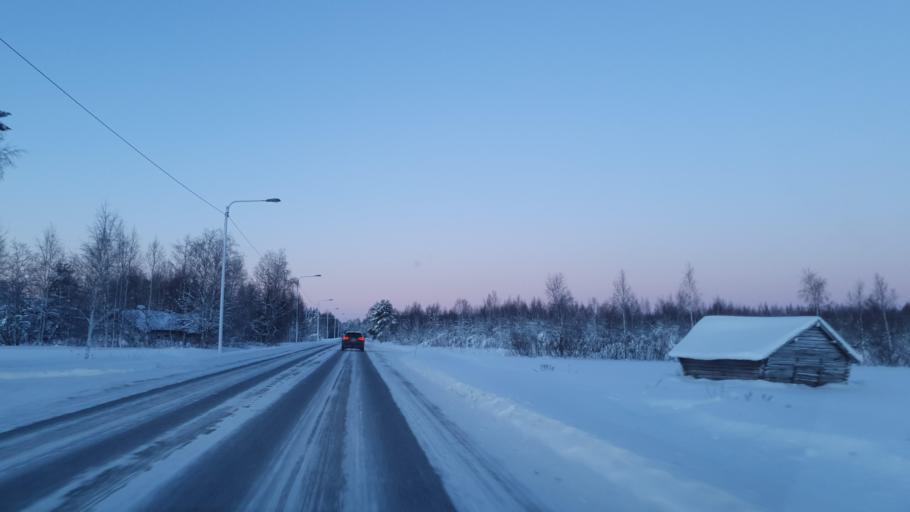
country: FI
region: Lapland
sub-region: Kemi-Tornio
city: Tornio
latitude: 66.0711
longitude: 23.9848
